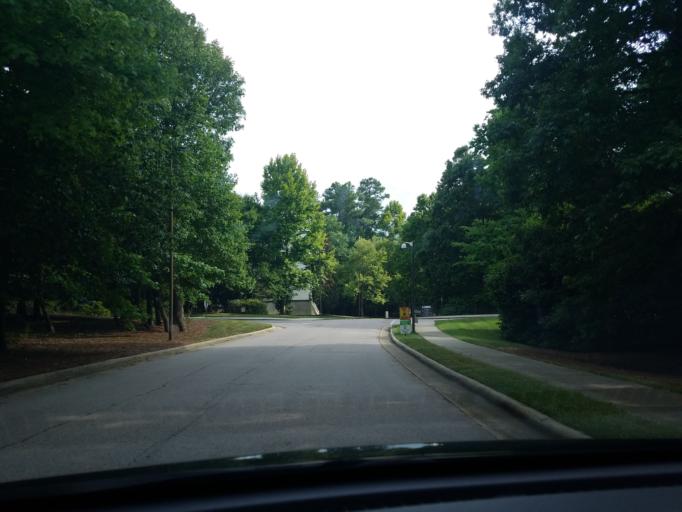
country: US
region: North Carolina
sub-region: Wake County
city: Apex
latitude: 35.7316
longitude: -78.8090
